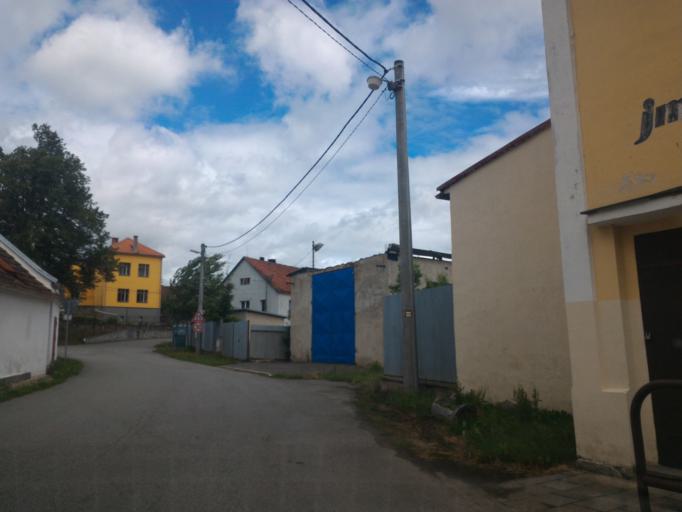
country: CZ
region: Vysocina
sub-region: Okres Jihlava
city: Telc
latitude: 49.2364
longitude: 15.4350
